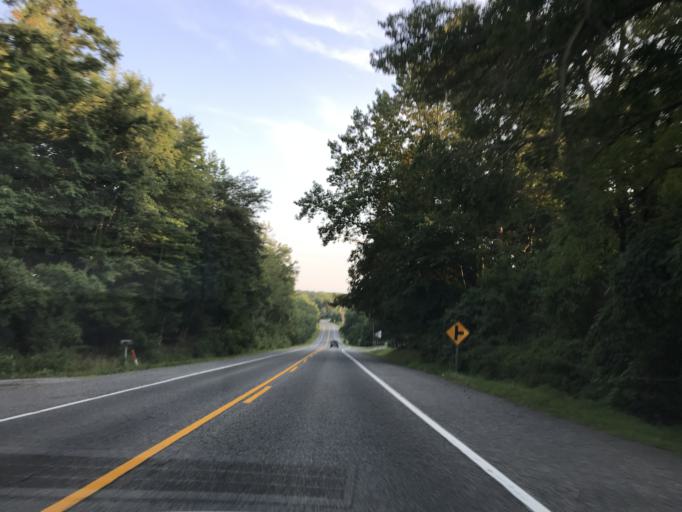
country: US
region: Maryland
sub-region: Cecil County
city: Charlestown
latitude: 39.5241
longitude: -75.9540
